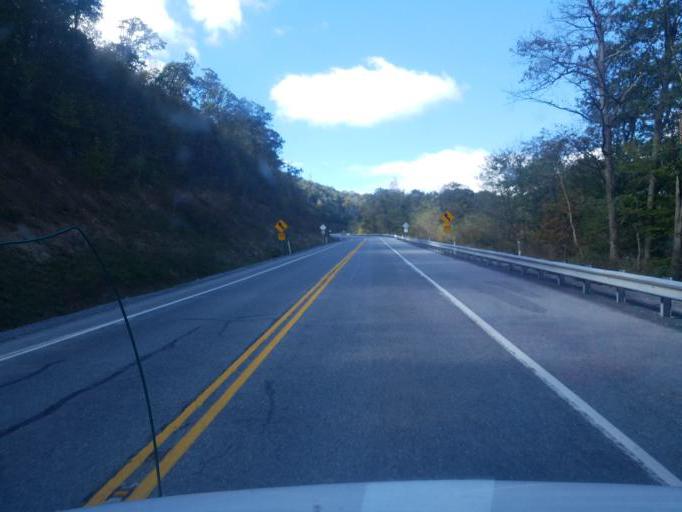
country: US
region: Pennsylvania
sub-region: Fulton County
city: McConnellsburg
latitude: 40.0154
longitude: -78.1372
